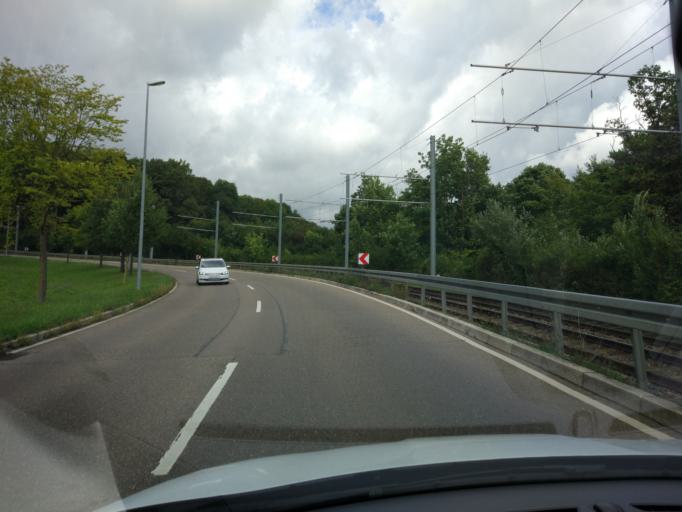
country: DE
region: Bavaria
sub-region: Swabia
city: Neu-Ulm
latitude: 48.4219
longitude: 10.0193
